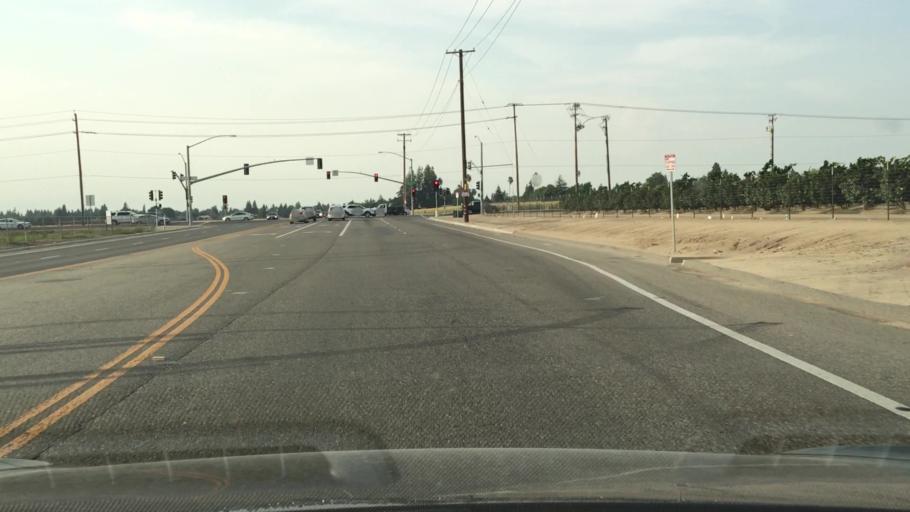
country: US
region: California
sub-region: Fresno County
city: Clovis
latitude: 36.8219
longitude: -119.7360
